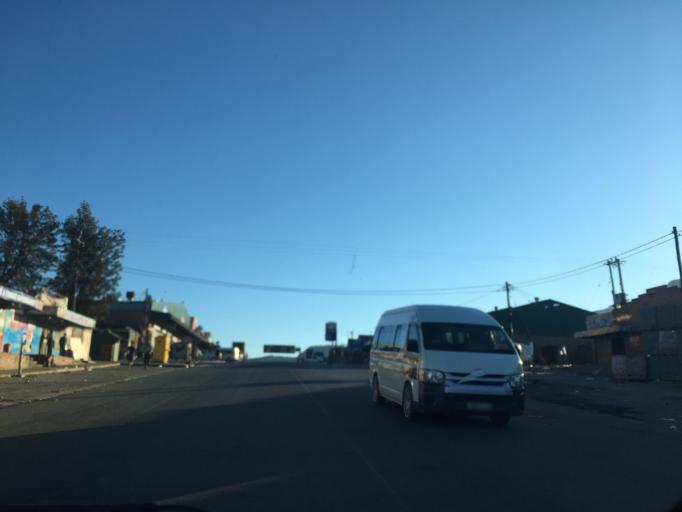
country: ZA
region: Eastern Cape
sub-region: Chris Hani District Municipality
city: Cala
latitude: -31.5263
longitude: 27.6943
